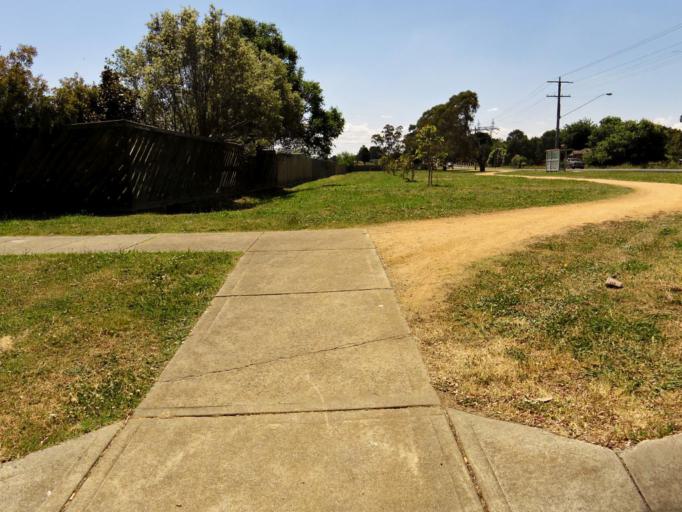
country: AU
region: Victoria
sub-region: Casey
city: Narre Warren South
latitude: -38.0380
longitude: 145.2879
